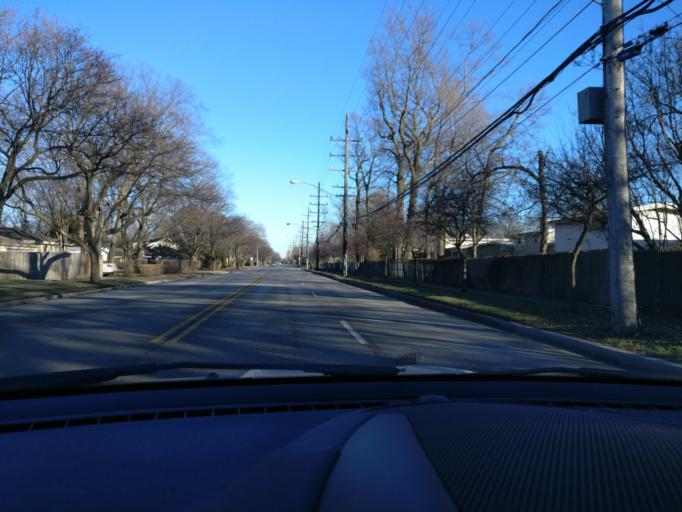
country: US
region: Illinois
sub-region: Cook County
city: Skokie
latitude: 42.0480
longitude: -87.7252
